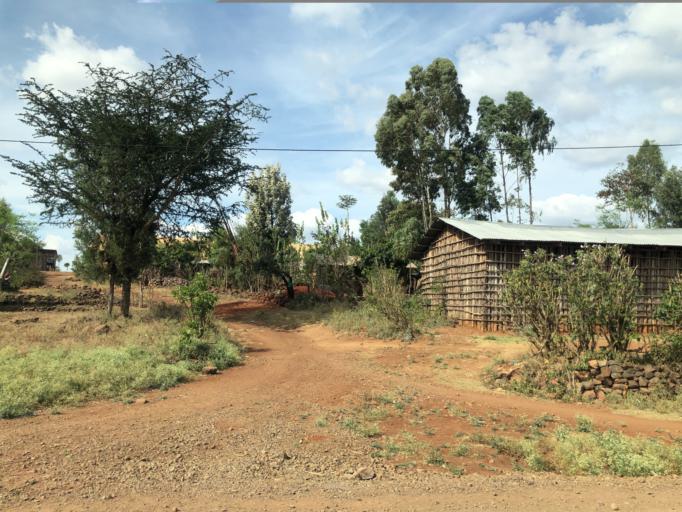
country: ET
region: Southern Nations, Nationalities, and People's Region
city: Konso
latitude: 5.3301
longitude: 37.4081
